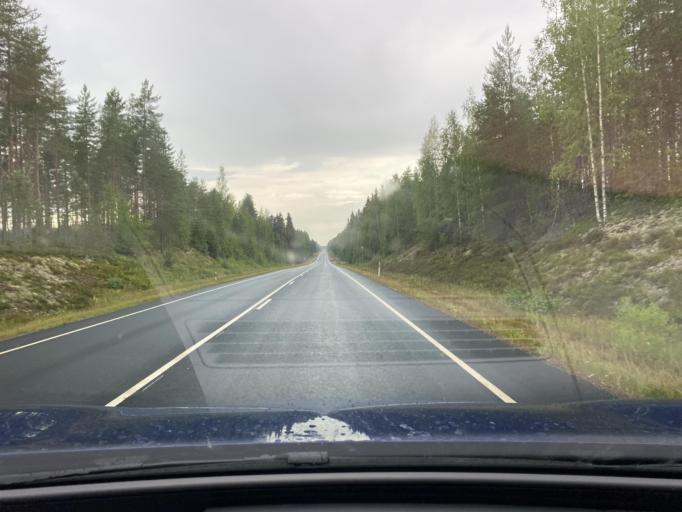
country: FI
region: Central Ostrobothnia
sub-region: Kaustinen
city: Veteli
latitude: 63.4144
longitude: 23.9496
